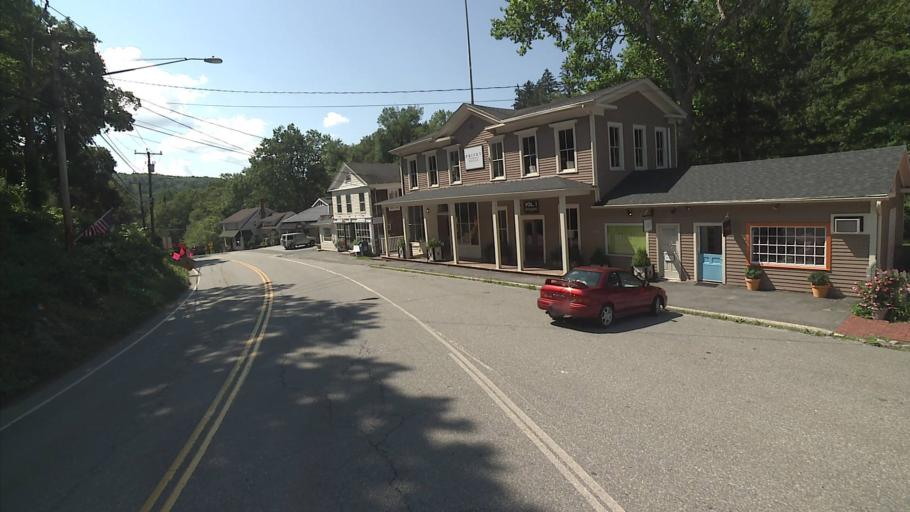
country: US
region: Connecticut
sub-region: Litchfield County
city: New Preston
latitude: 41.6766
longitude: -73.3557
